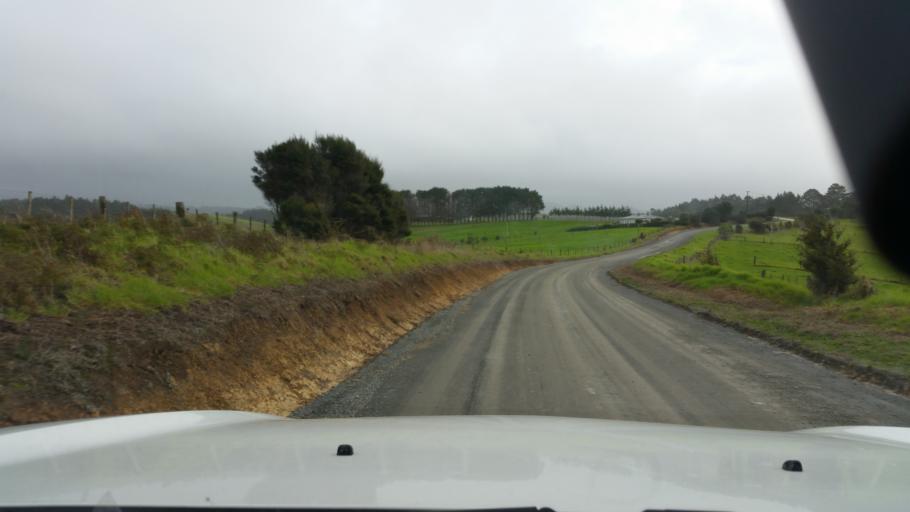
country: NZ
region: Northland
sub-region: Whangarei
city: Ngunguru
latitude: -35.7484
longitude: 174.5063
